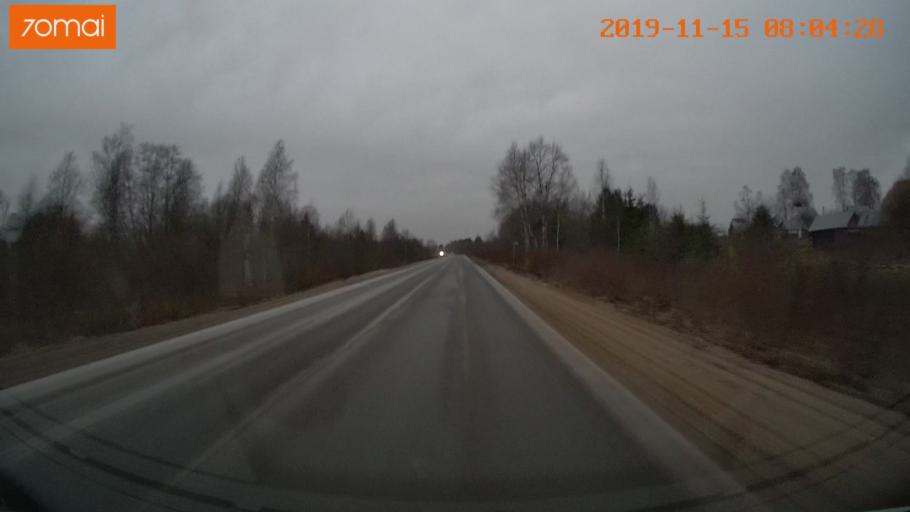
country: RU
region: Vologda
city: Cherepovets
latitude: 59.0086
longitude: 38.0754
